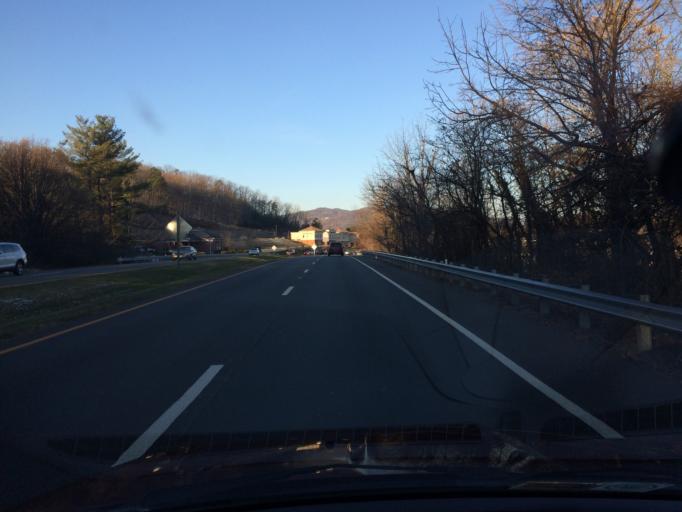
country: US
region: Virginia
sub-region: Roanoke County
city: Cave Spring
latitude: 37.2247
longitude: -79.9932
